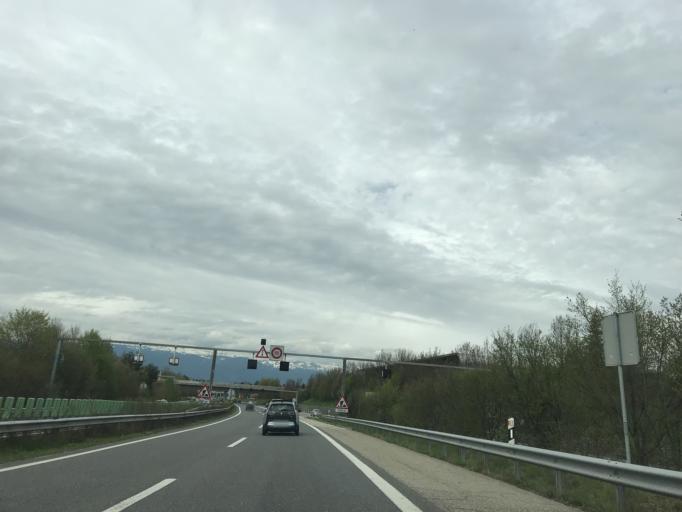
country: CH
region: Geneva
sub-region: Geneva
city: Confignon
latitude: 46.1638
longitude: 6.1004
